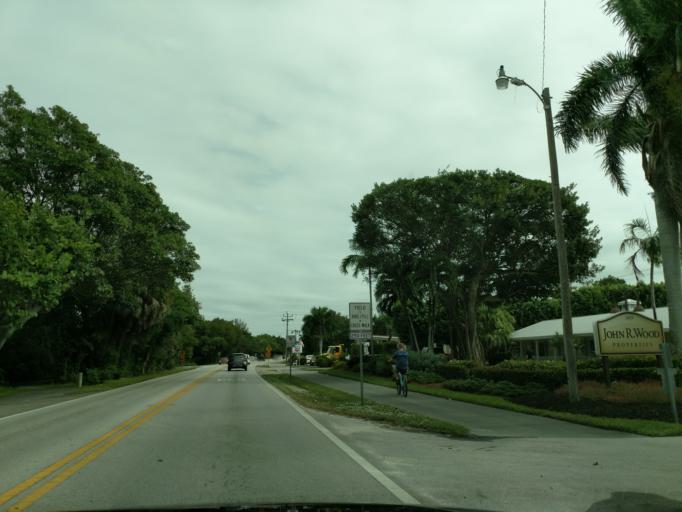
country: US
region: Florida
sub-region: Lee County
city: Sanibel
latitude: 26.4465
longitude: -82.0409
